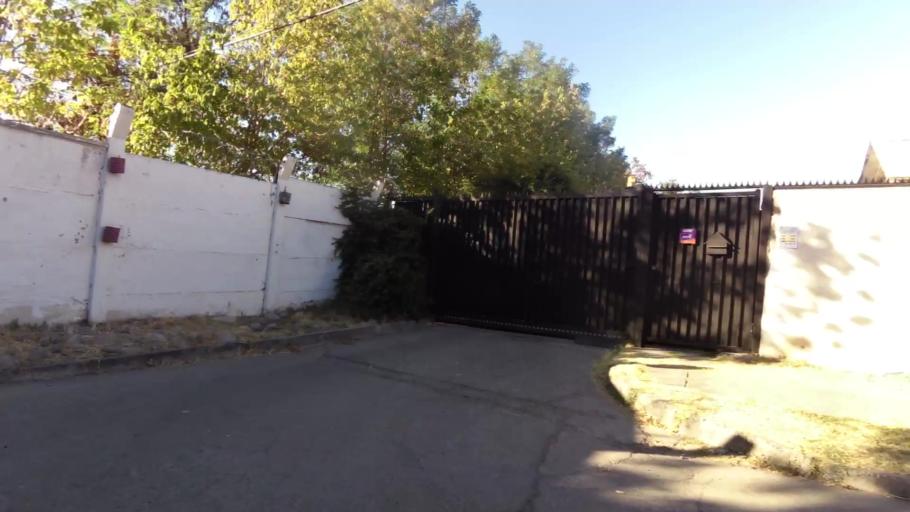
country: CL
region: O'Higgins
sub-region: Provincia de Cachapoal
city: Rancagua
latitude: -34.1714
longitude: -70.7212
